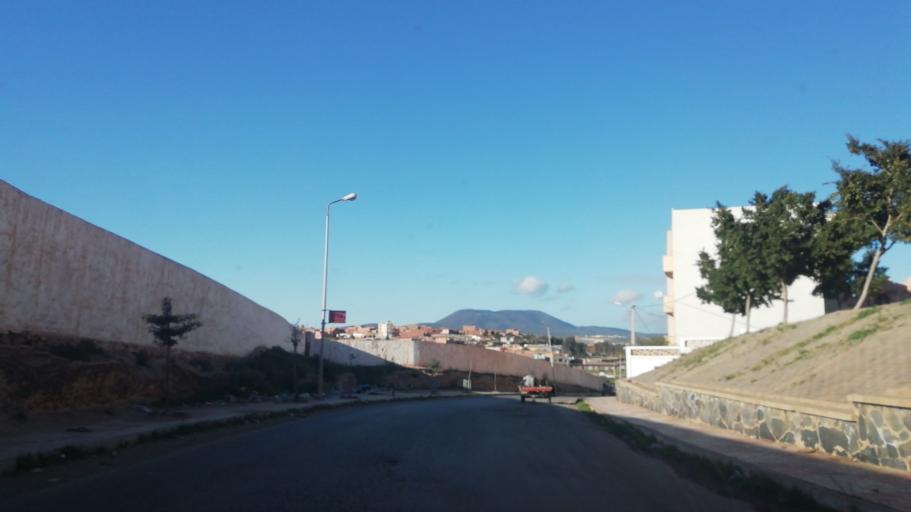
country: DZ
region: Oran
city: Sidi ech Chahmi
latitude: 35.6949
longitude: -0.4945
